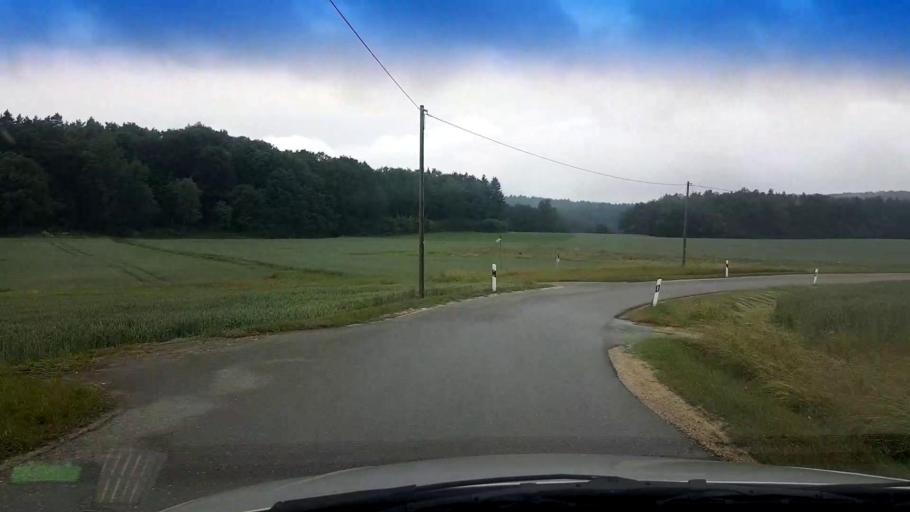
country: DE
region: Bavaria
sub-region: Upper Franconia
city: Altendorf
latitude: 50.0643
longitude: 11.1518
